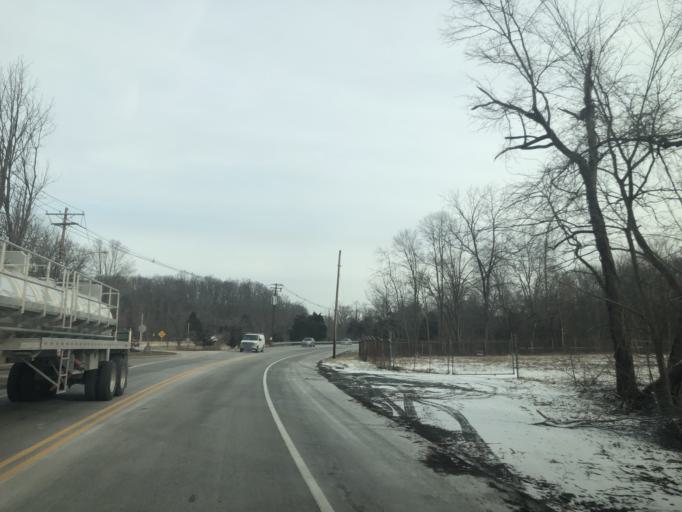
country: US
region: New Jersey
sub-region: Warren County
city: Oxford
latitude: 40.9195
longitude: -74.9660
